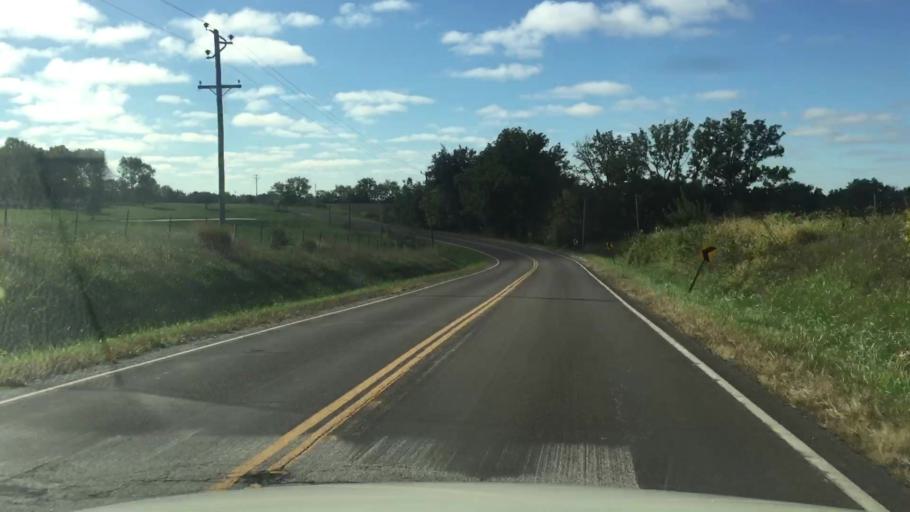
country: US
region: Missouri
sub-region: Howard County
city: New Franklin
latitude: 39.0651
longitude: -92.7462
